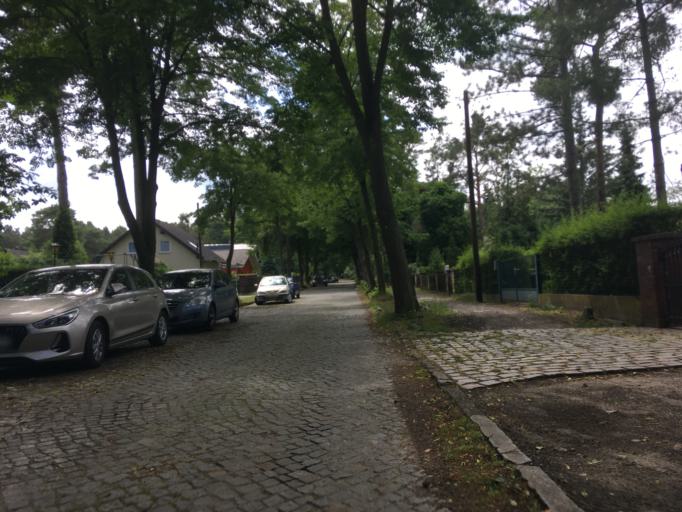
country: DE
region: Berlin
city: Muggelheim
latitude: 52.4068
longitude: 13.6584
